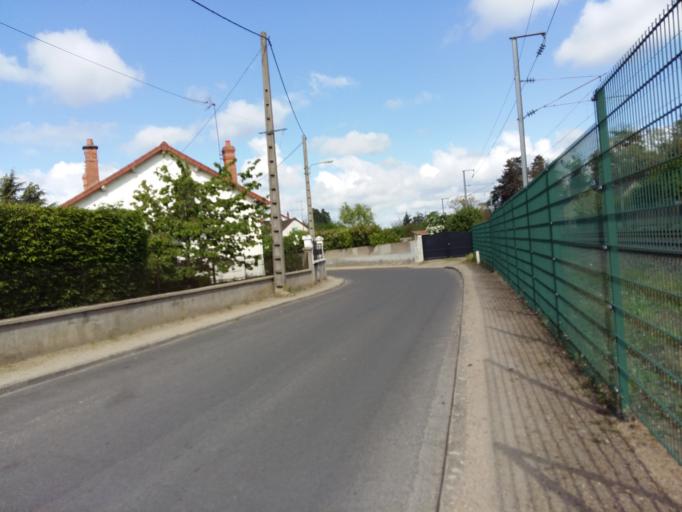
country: FR
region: Auvergne
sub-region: Departement de l'Allier
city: Moulins
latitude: 46.5720
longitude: 3.3394
